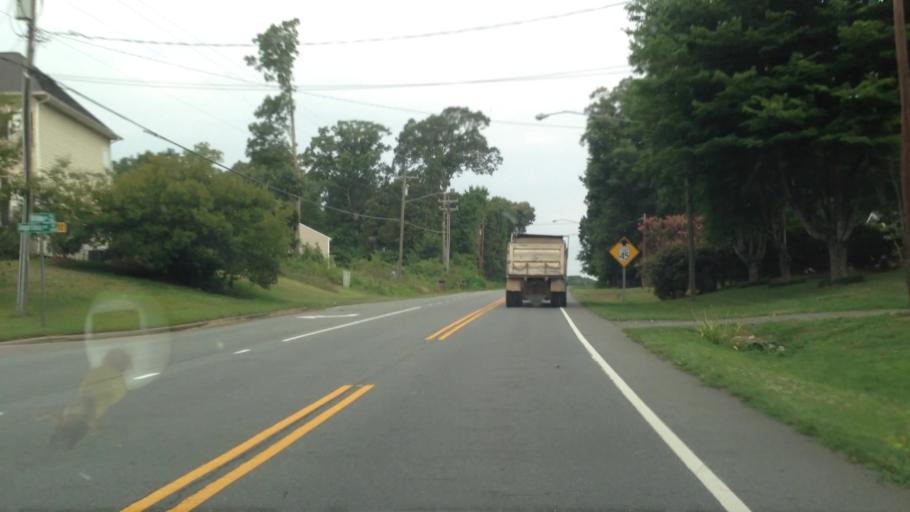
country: US
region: North Carolina
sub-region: Forsyth County
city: Rural Hall
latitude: 36.1972
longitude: -80.2681
